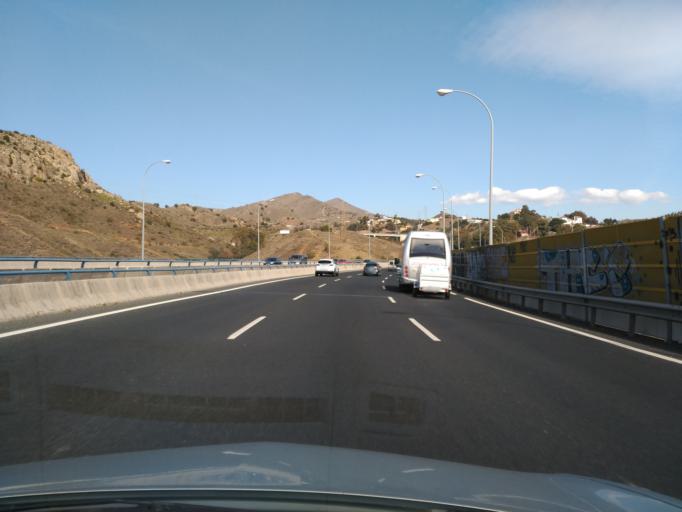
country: ES
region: Andalusia
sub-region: Provincia de Malaga
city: Malaga
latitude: 36.7364
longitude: -4.4541
